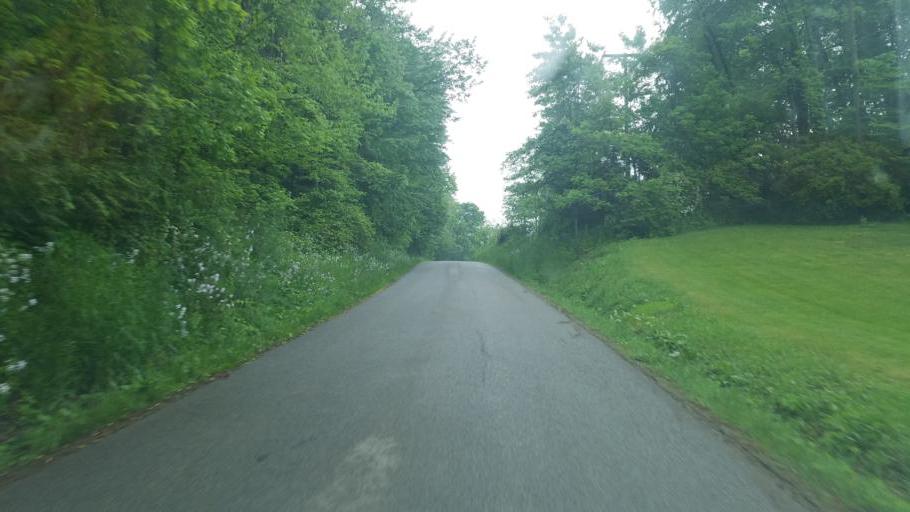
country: US
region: Ohio
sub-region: Richland County
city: Lincoln Heights
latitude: 40.7095
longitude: -82.4242
